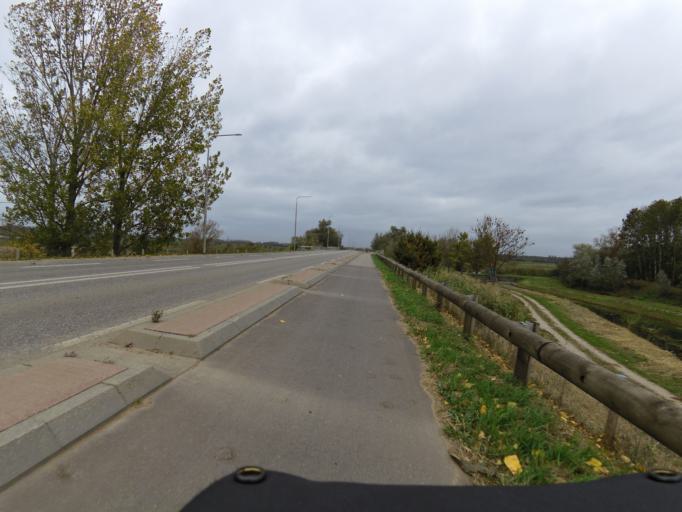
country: NL
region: Gelderland
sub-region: Gemeente Zevenaar
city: Zevenaar
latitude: 51.8904
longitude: 6.1017
